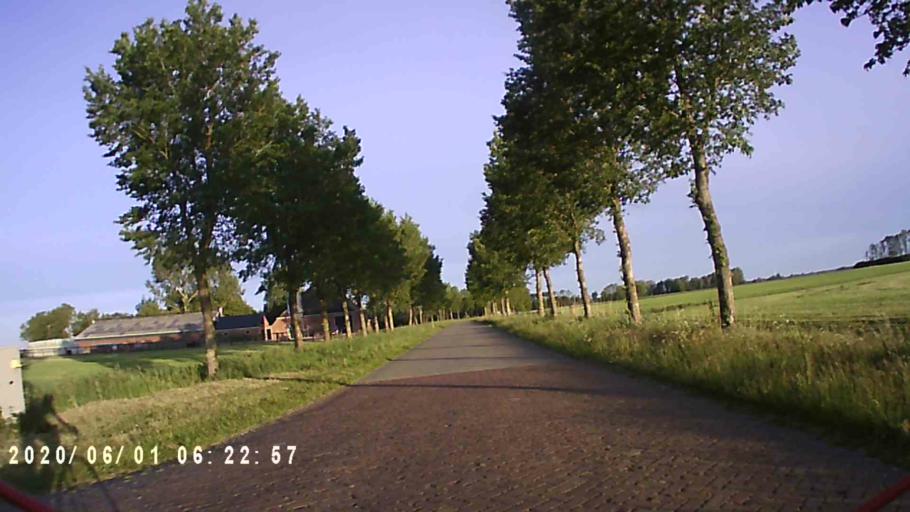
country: NL
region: Friesland
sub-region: Gemeente Kollumerland en Nieuwkruisland
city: Kollum
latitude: 53.2654
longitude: 6.2187
